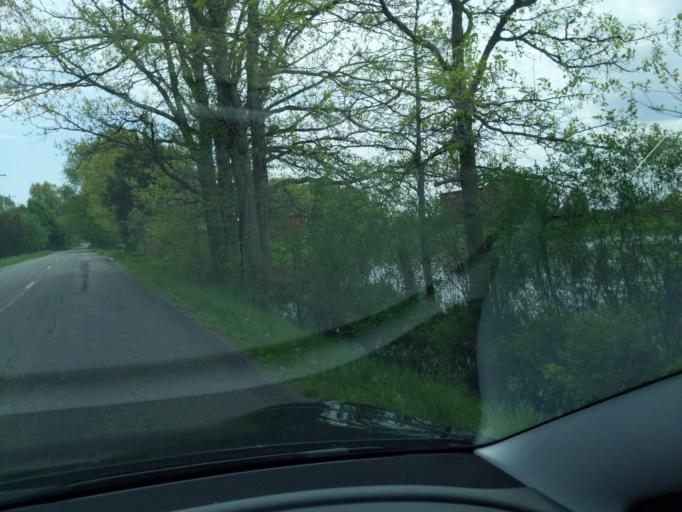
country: US
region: Michigan
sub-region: Ingham County
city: Stockbridge
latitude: 42.4594
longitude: -84.2246
